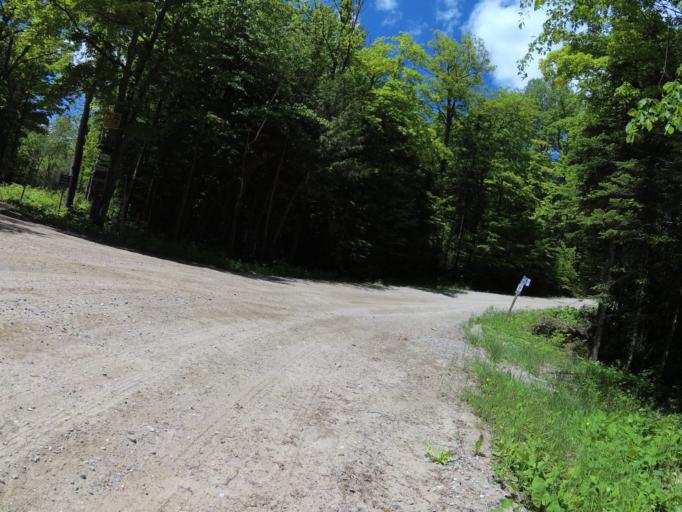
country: CA
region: Ontario
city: Renfrew
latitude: 44.9981
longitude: -76.9152
